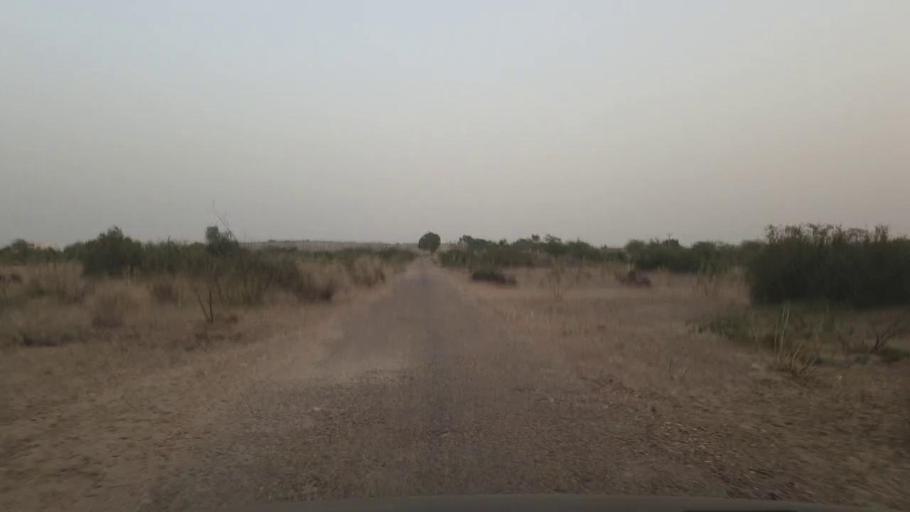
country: PK
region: Sindh
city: Chor
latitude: 25.5013
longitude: 69.8222
